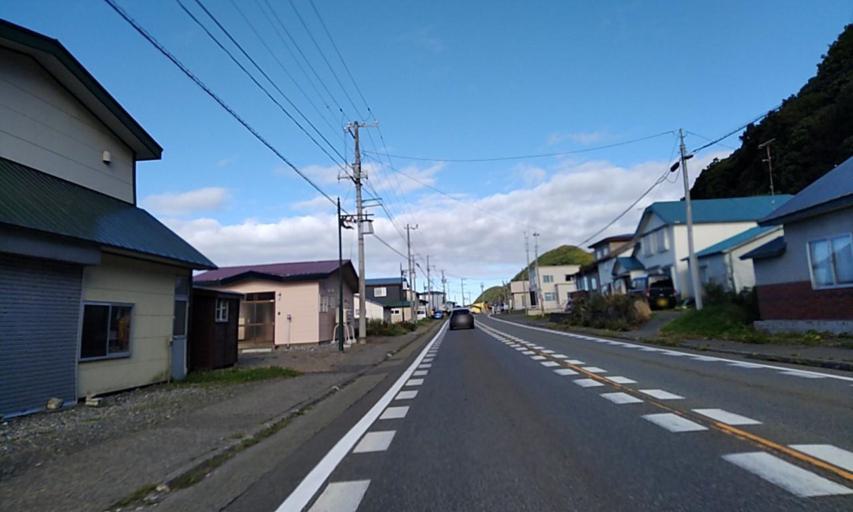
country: JP
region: Hokkaido
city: Shizunai-furukawacho
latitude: 42.2521
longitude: 142.5419
